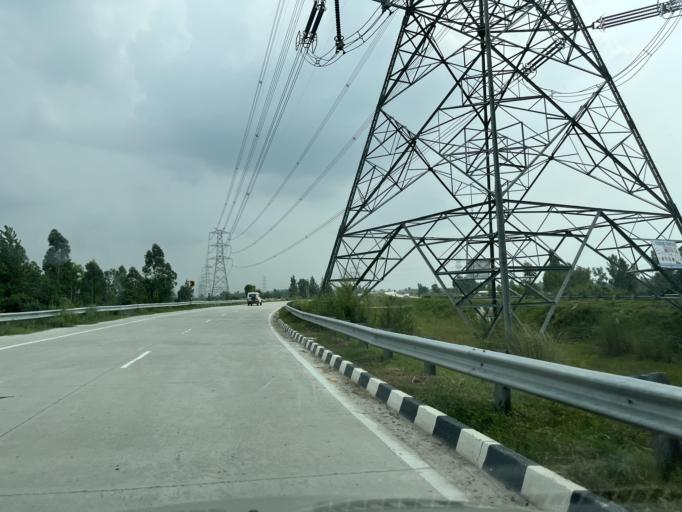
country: IN
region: Uttarakhand
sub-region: Udham Singh Nagar
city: Jaspur
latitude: 29.2778
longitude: 78.8680
